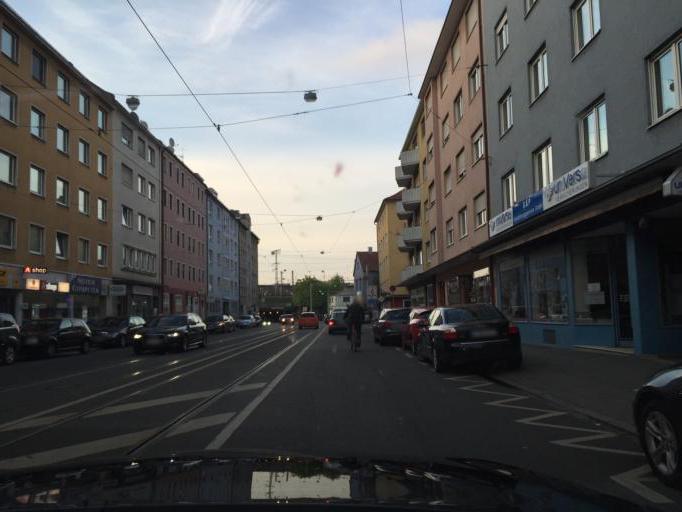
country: DE
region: Bavaria
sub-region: Regierungsbezirk Mittelfranken
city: Nuernberg
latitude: 49.4406
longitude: 11.0675
